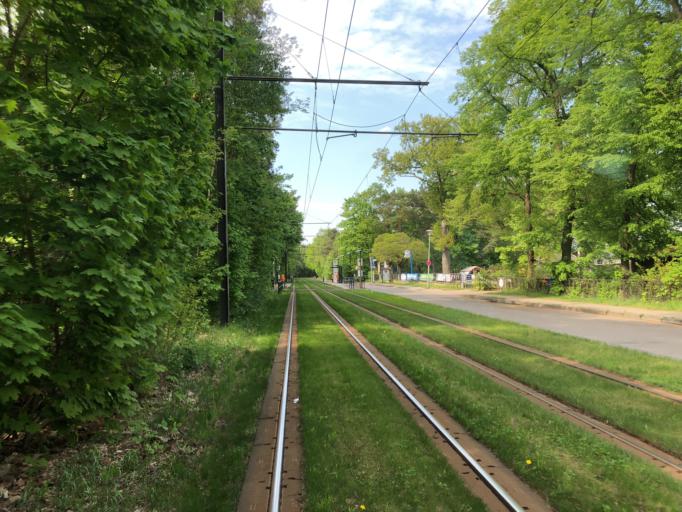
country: DE
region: Brandenburg
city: Zeuthen
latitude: 52.4009
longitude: 13.6251
